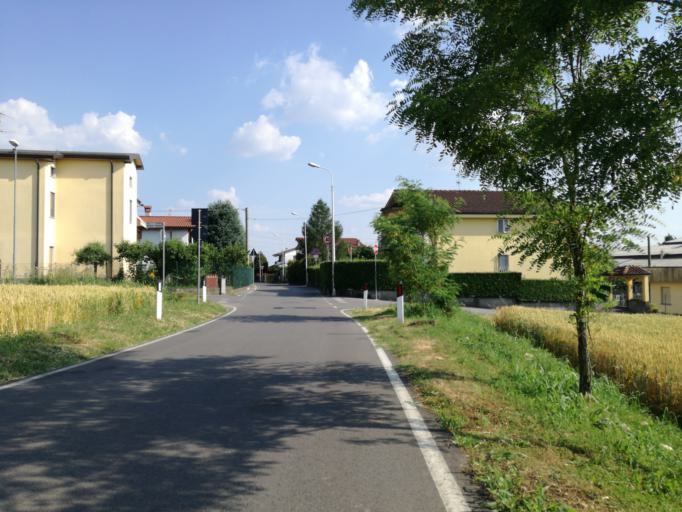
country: IT
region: Lombardy
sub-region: Provincia di Bergamo
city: Calusco d'Adda
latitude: 45.6868
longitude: 9.4581
